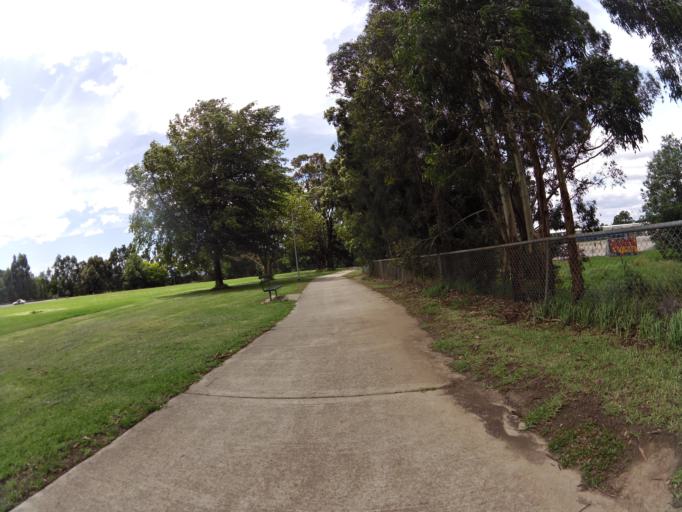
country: AU
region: Victoria
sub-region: Latrobe
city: Traralgon
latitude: -38.1889
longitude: 146.5367
